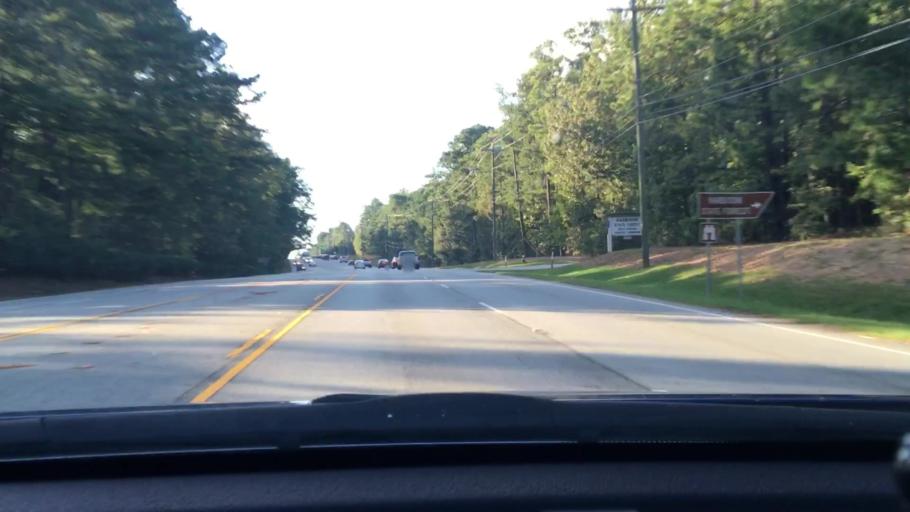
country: US
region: South Carolina
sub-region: Lexington County
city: Seven Oaks
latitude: 34.0817
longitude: -81.1342
